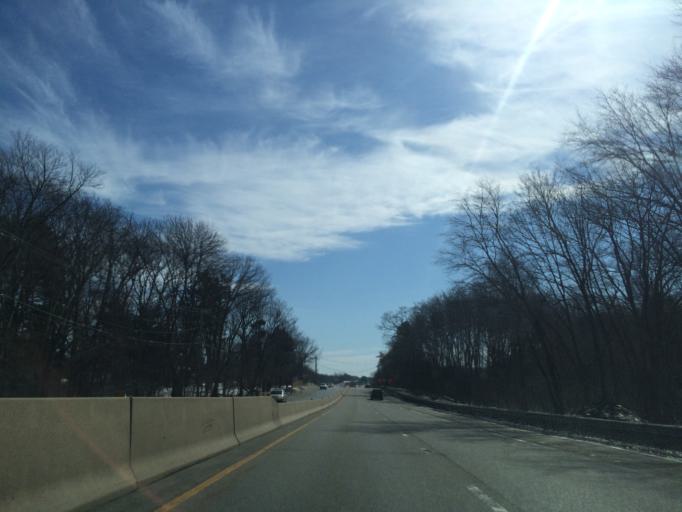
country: US
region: Massachusetts
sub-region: Middlesex County
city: Lincoln
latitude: 42.4332
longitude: -71.2690
